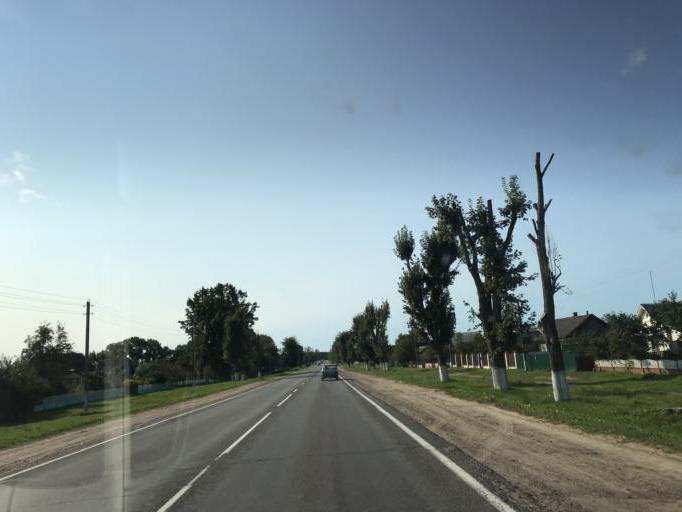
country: BY
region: Mogilev
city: Buynichy
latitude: 53.8325
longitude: 30.2447
